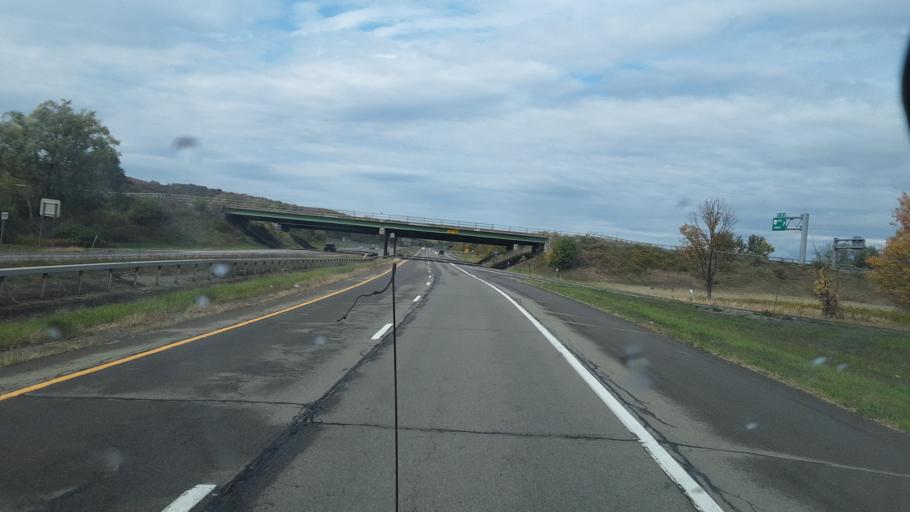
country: US
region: New York
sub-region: Steuben County
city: Hornell
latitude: 42.3693
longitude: -77.6756
